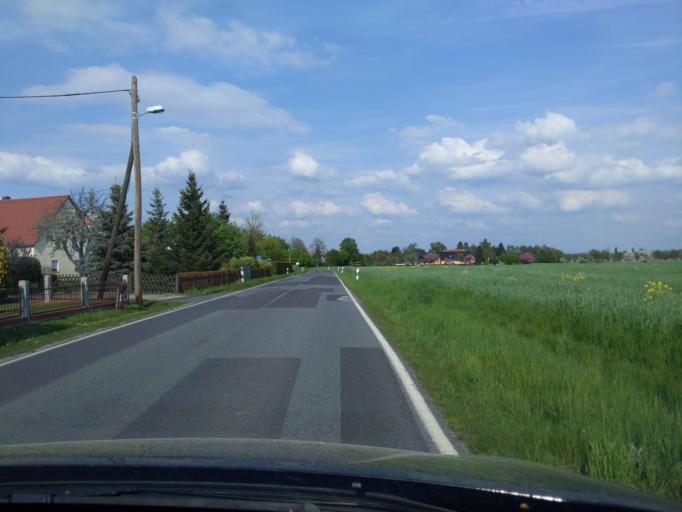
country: DE
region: Saxony
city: Malschwitz
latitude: 51.2005
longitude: 14.5200
